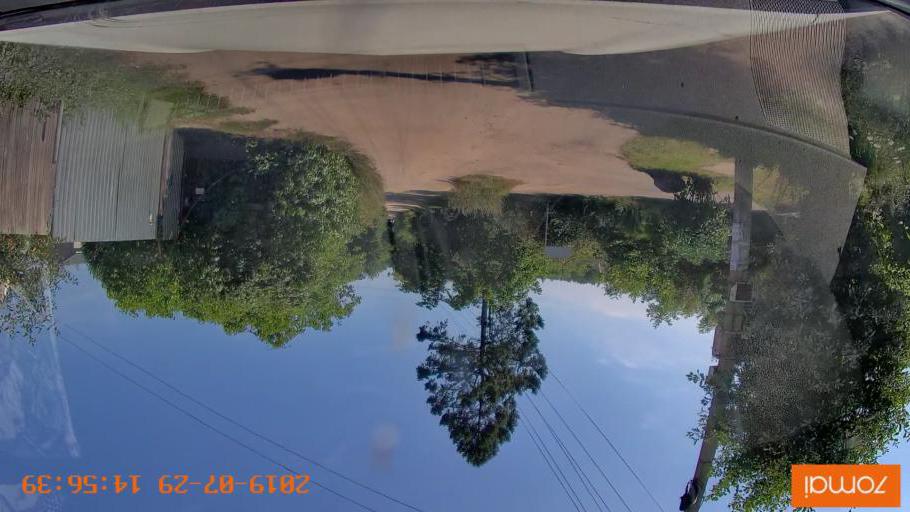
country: RU
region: Kaliningrad
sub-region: Gorod Kaliningrad
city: Baltiysk
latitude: 54.6802
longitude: 19.9194
